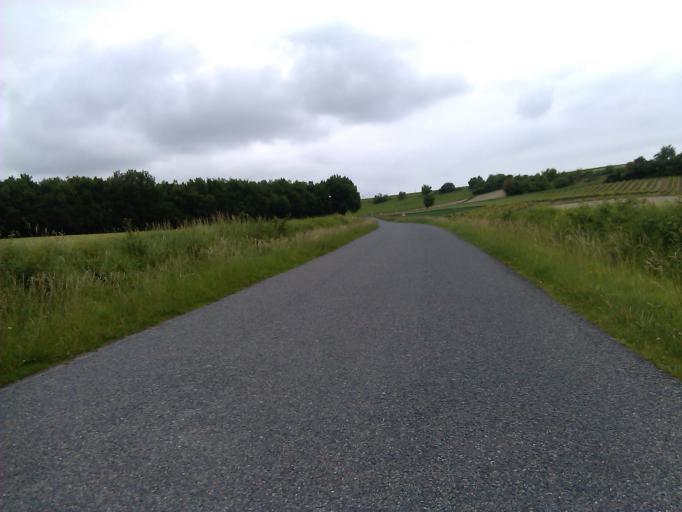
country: FR
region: Poitou-Charentes
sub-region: Departement de la Charente
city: Chateauneuf-sur-Charente
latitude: 45.5551
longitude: -0.0693
